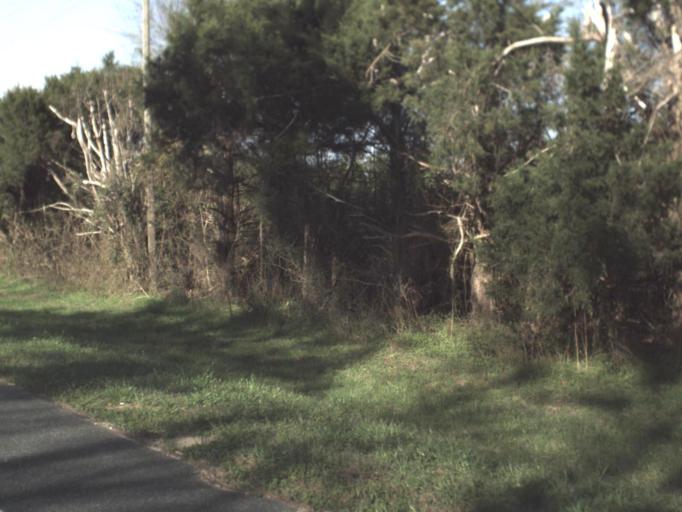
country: US
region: Florida
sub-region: Calhoun County
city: Blountstown
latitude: 30.4940
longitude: -85.2001
